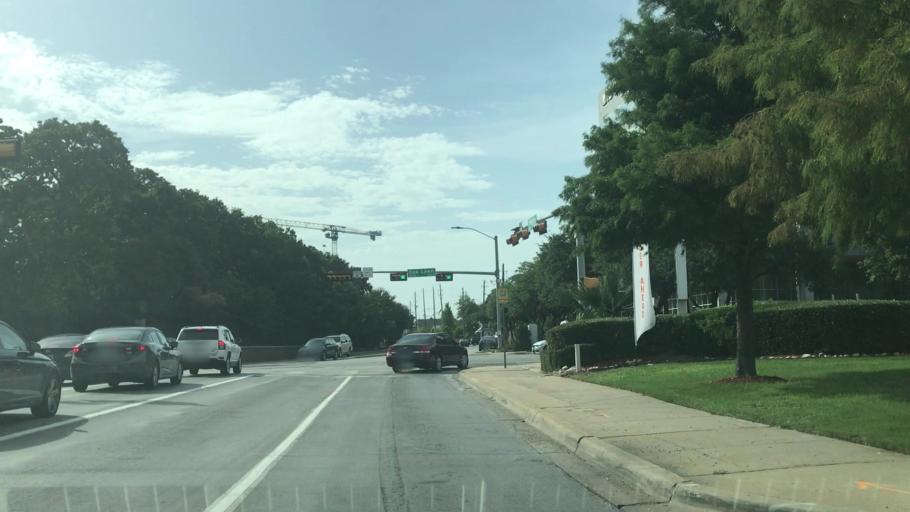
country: US
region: Texas
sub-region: Dallas County
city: Dallas
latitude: 32.8039
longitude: -96.8140
